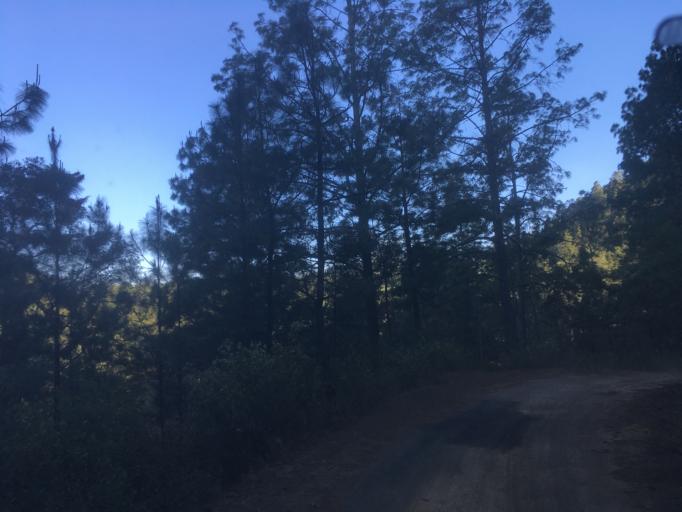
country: MX
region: Michoacan
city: Angahuan
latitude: 19.4759
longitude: -102.2424
